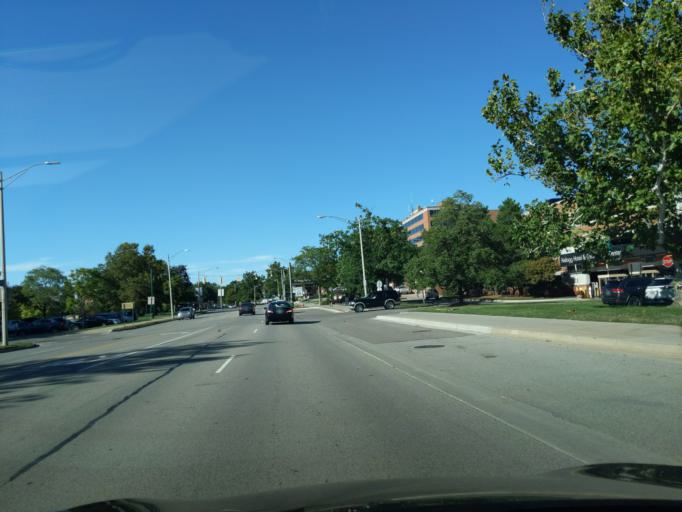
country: US
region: Michigan
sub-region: Ingham County
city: East Lansing
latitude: 42.7301
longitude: -84.4939
